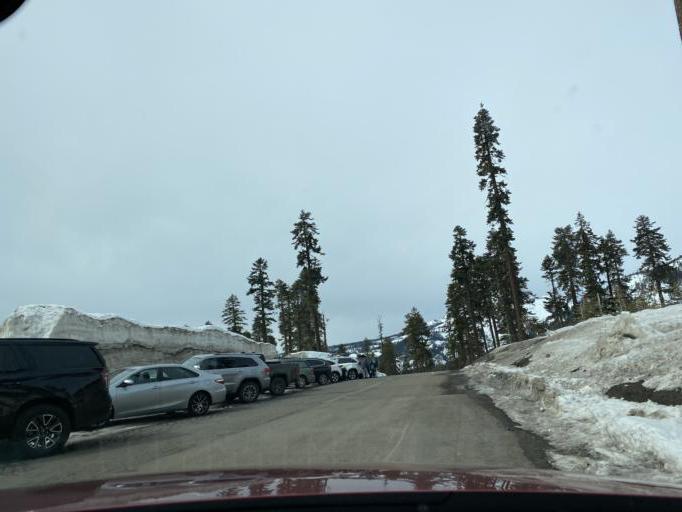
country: US
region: California
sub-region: El Dorado County
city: South Lake Tahoe
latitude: 38.8012
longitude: -120.0828
